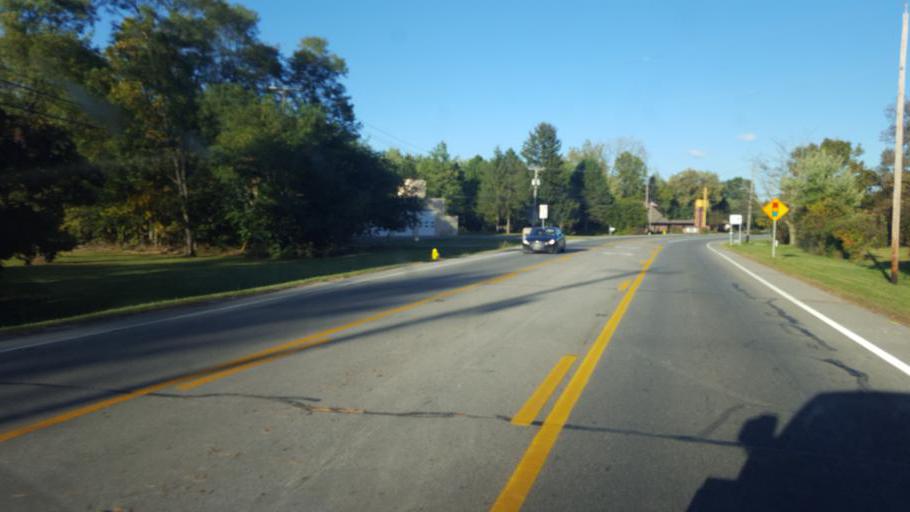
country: US
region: Ohio
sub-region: Franklin County
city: Gahanna
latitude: 40.0189
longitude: -82.8176
